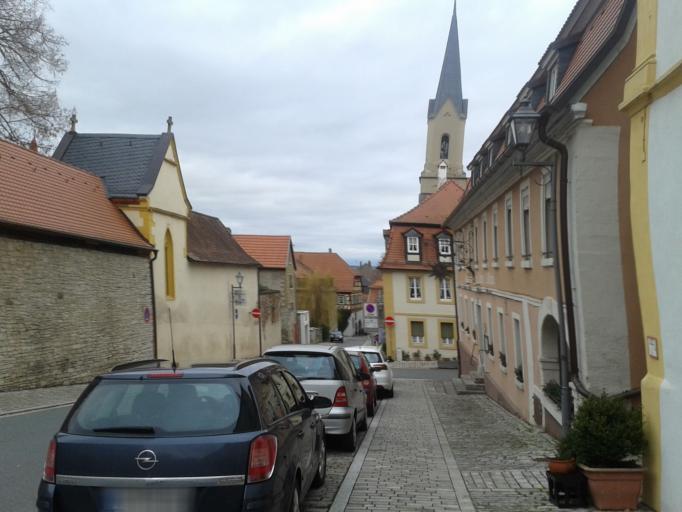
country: DE
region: Bavaria
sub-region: Regierungsbezirk Unterfranken
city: Marktbreit
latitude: 49.6655
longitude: 10.1434
